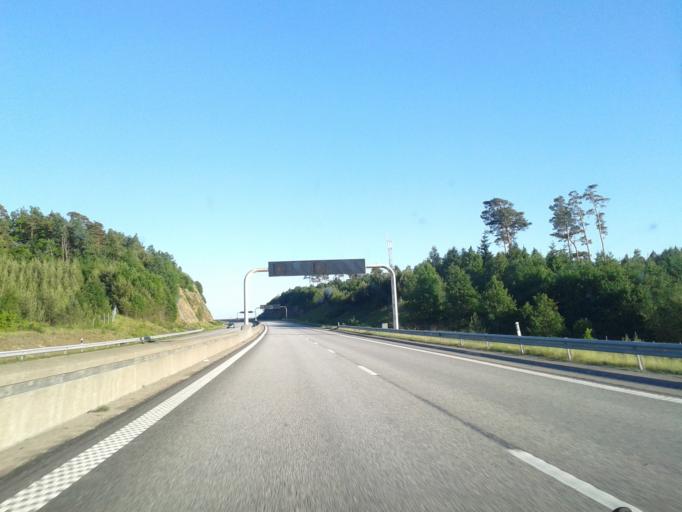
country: SE
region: Vaestra Goetaland
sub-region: Uddevalla Kommun
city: Uddevalla
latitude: 58.3354
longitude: 11.8290
